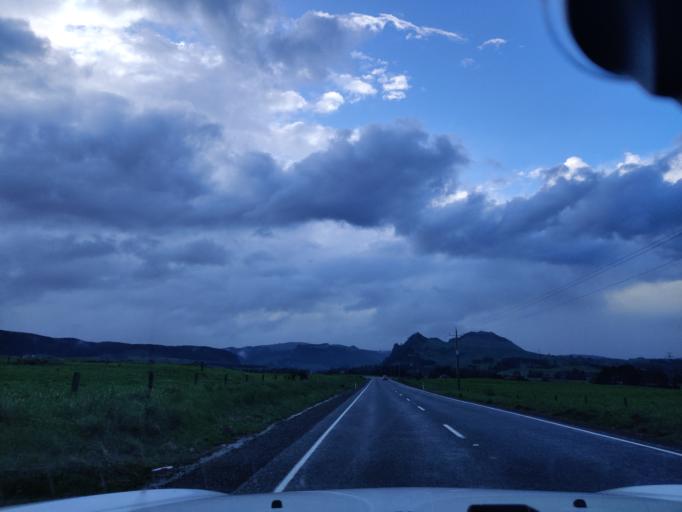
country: NZ
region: Waikato
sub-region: South Waikato District
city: Tokoroa
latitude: -38.4037
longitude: 175.7910
